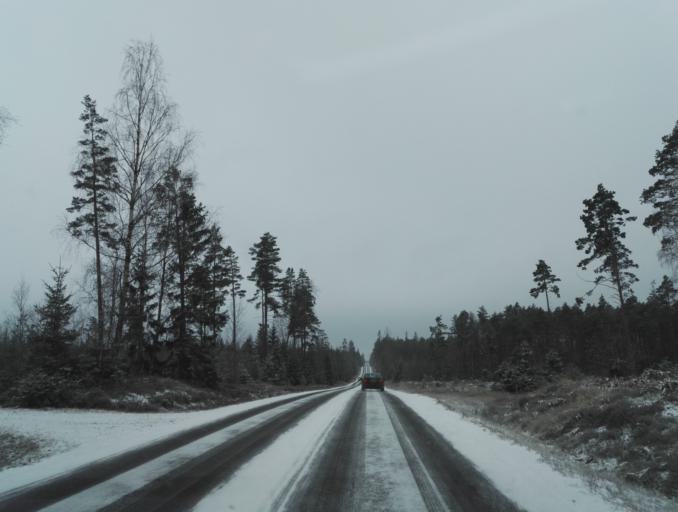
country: SE
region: Kronoberg
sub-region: Lessebo Kommun
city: Lessebo
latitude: 56.7723
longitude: 15.2974
